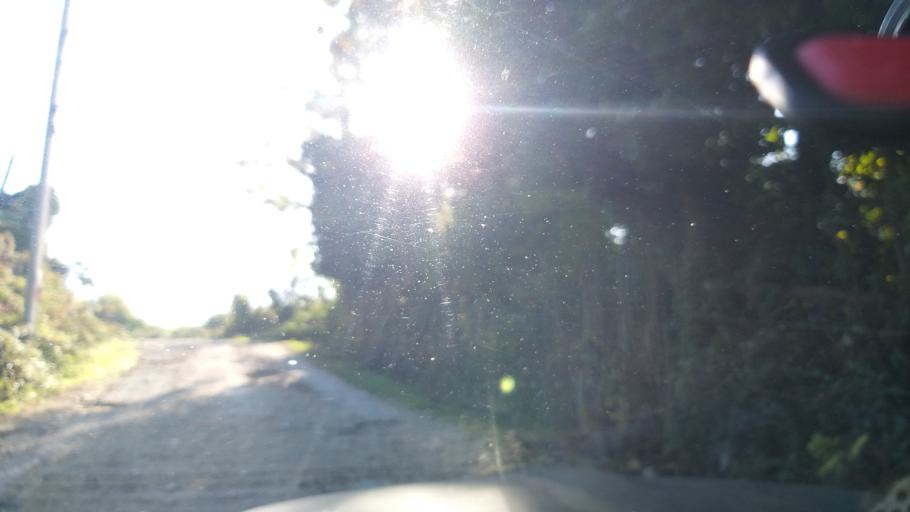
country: GE
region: Abkhazia
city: Stantsiya Novyy Afon
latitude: 43.0651
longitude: 40.8828
